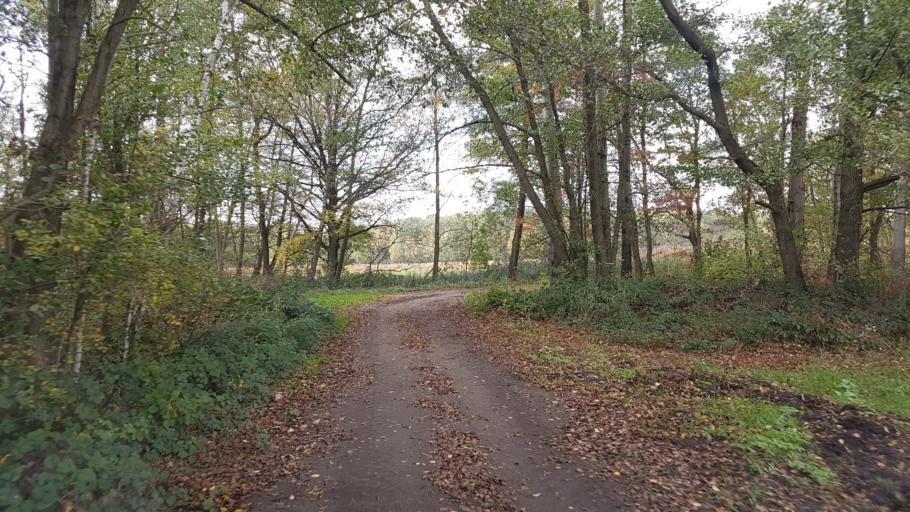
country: DE
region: Brandenburg
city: Schonborn
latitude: 51.5756
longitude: 13.4953
